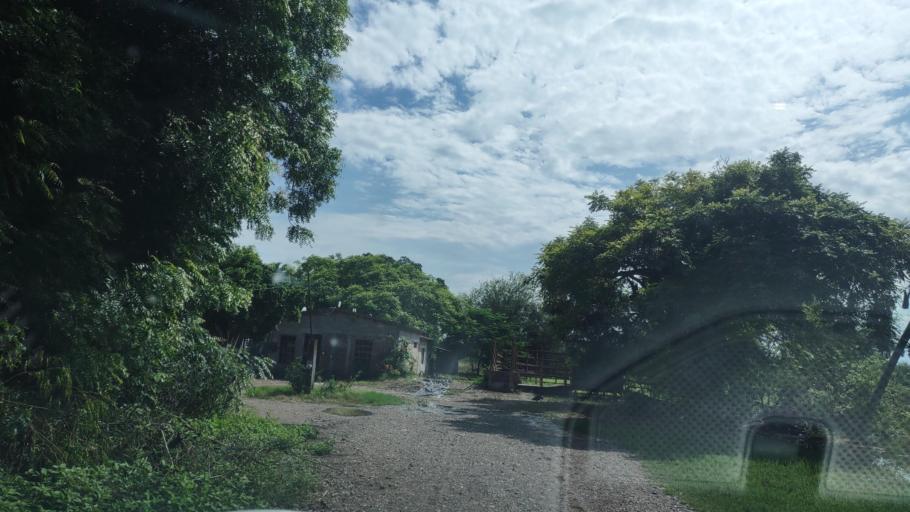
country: MX
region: Veracruz
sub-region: Panuco
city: Oviedo
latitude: 22.0005
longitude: -98.4580
